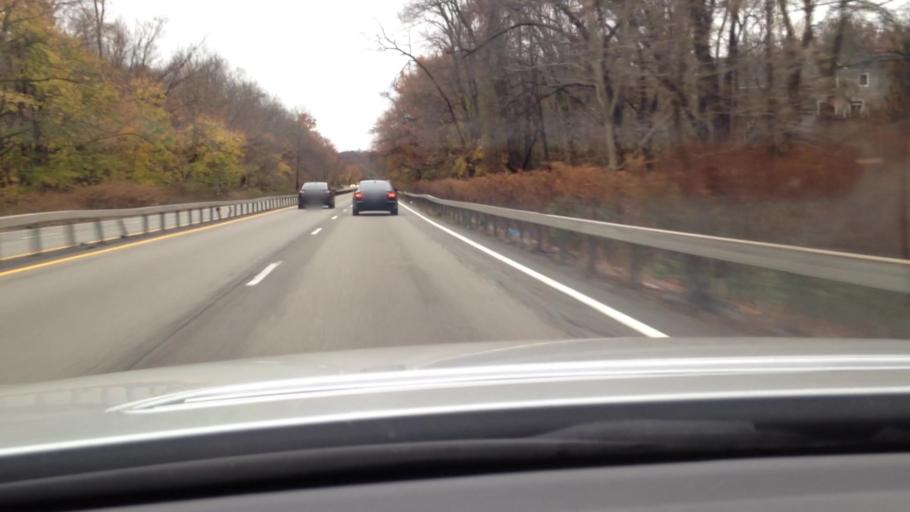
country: US
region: New York
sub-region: Westchester County
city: Briarcliff Manor
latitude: 41.1389
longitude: -73.8205
